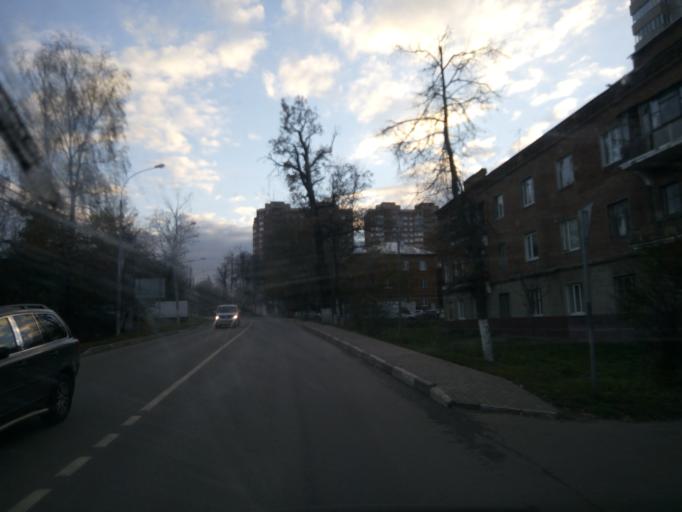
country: RU
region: Moskovskaya
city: Skhodnya
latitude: 55.9598
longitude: 37.3064
